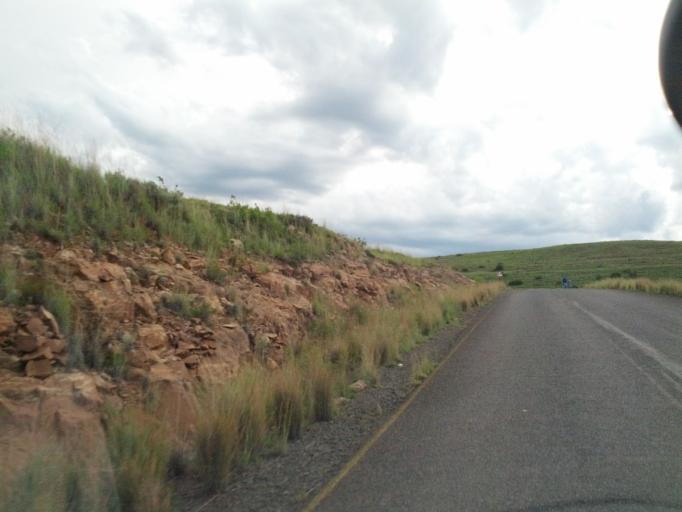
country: LS
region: Qacha's Nek
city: Qacha's Nek
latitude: -30.0530
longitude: 28.5004
